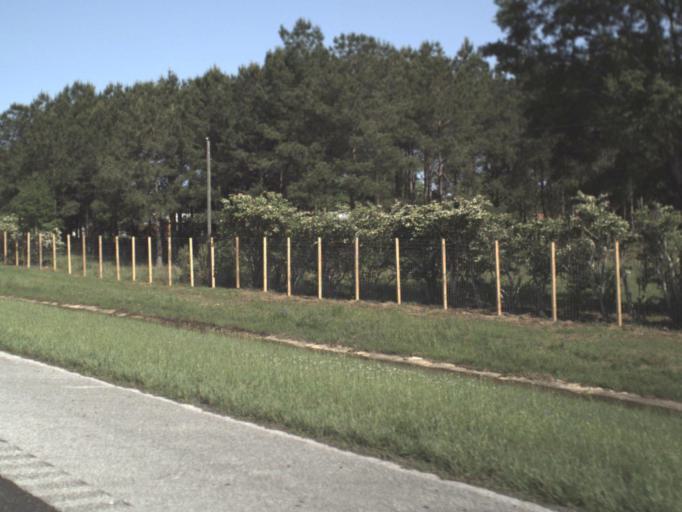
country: US
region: Florida
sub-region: Holmes County
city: Bonifay
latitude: 30.7623
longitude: -85.6653
